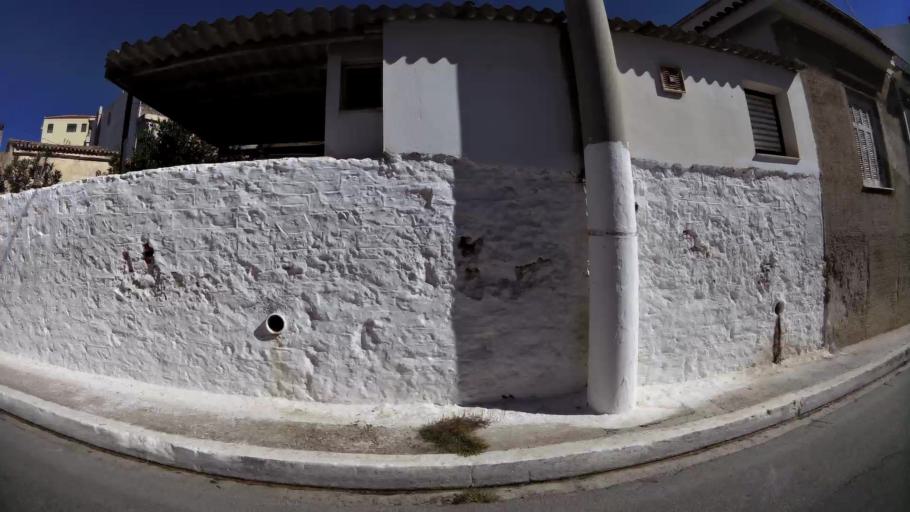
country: GR
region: Attica
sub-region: Nomarchia Anatolikis Attikis
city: Koropi
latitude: 37.8992
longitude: 23.8769
